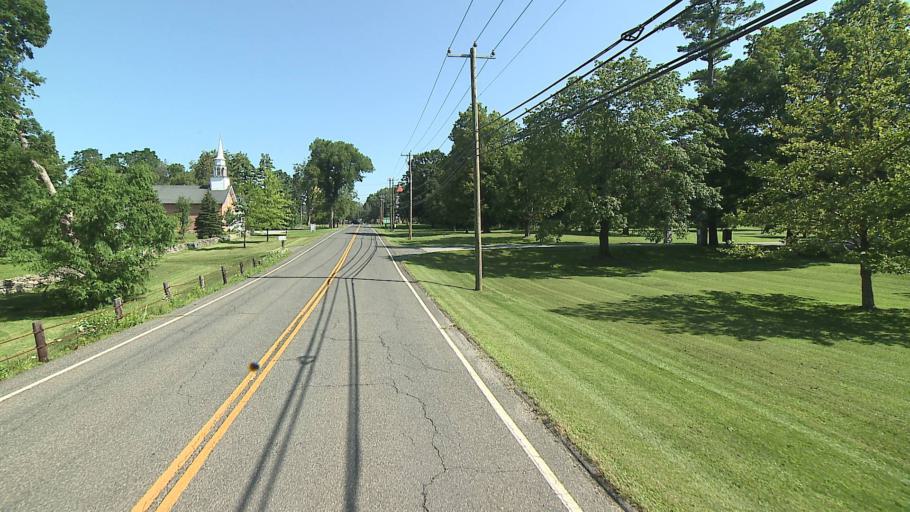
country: US
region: Connecticut
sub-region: Litchfield County
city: Kent
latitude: 41.8744
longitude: -73.4774
